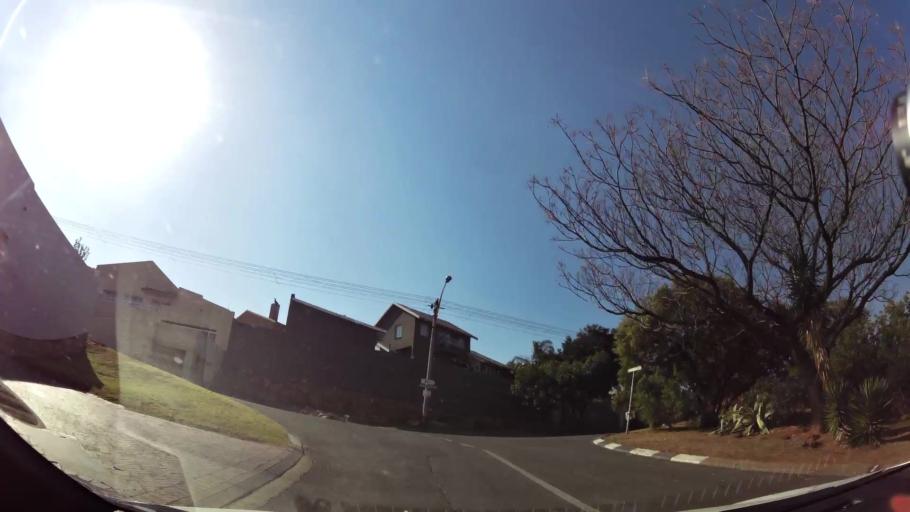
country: ZA
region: Gauteng
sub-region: City of Johannesburg Metropolitan Municipality
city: Johannesburg
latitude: -26.2679
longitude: 28.0426
